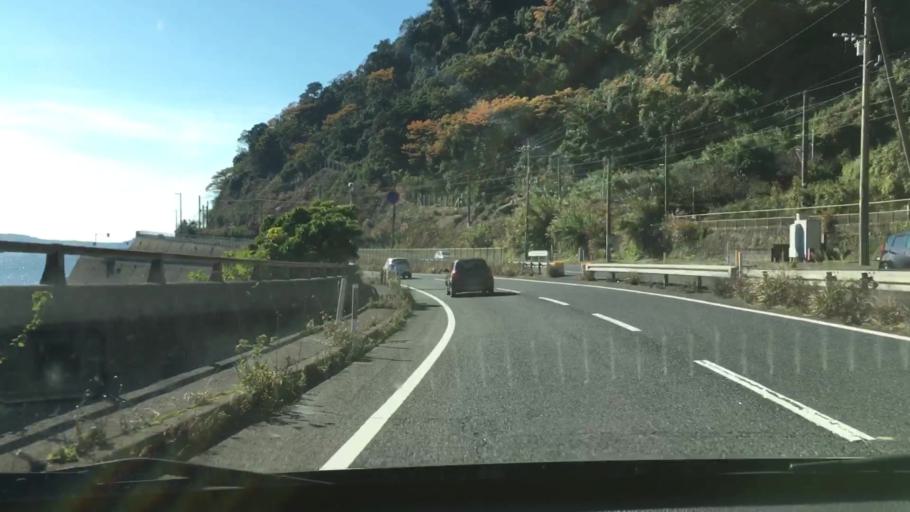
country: JP
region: Kagoshima
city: Kagoshima-shi
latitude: 31.6411
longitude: 130.6025
